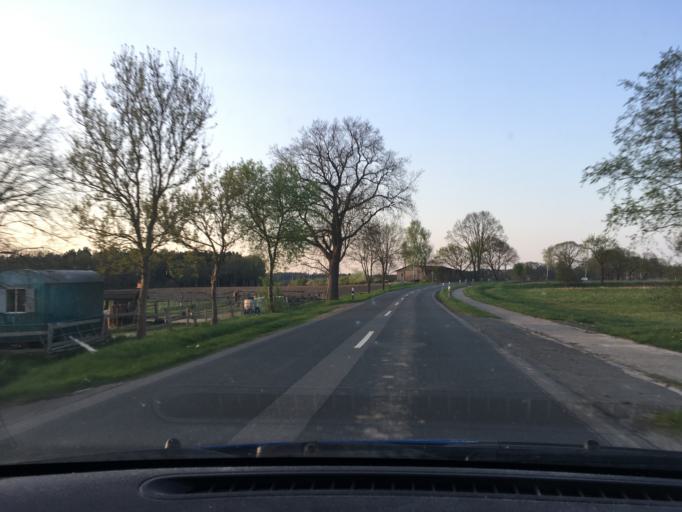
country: DE
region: Lower Saxony
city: Kirchgellersen
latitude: 53.2367
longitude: 10.2984
